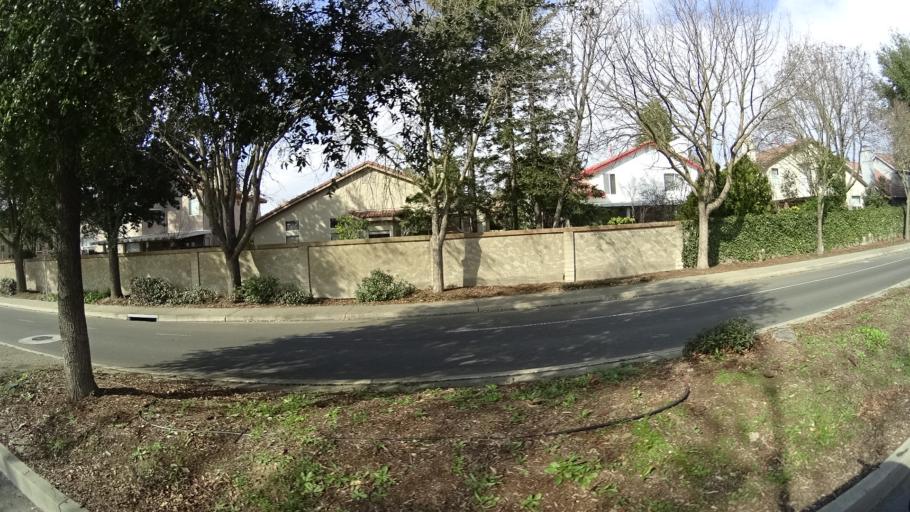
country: US
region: California
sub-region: Yolo County
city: Davis
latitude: 38.5539
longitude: -121.7116
